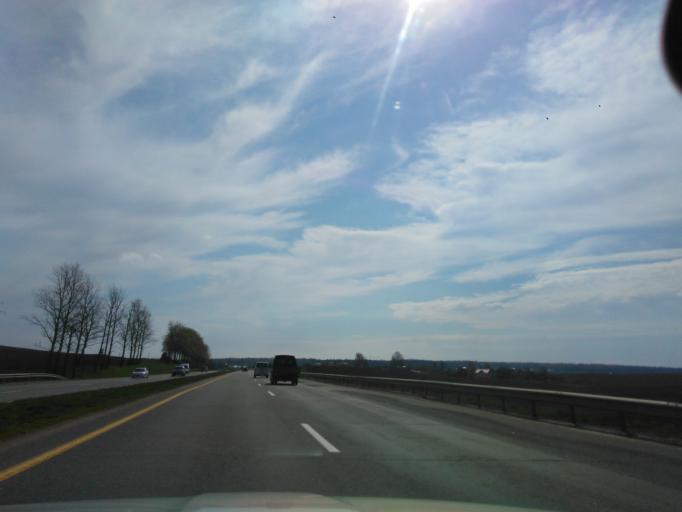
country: BY
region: Minsk
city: Novosel'ye
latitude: 53.9160
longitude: 27.2226
